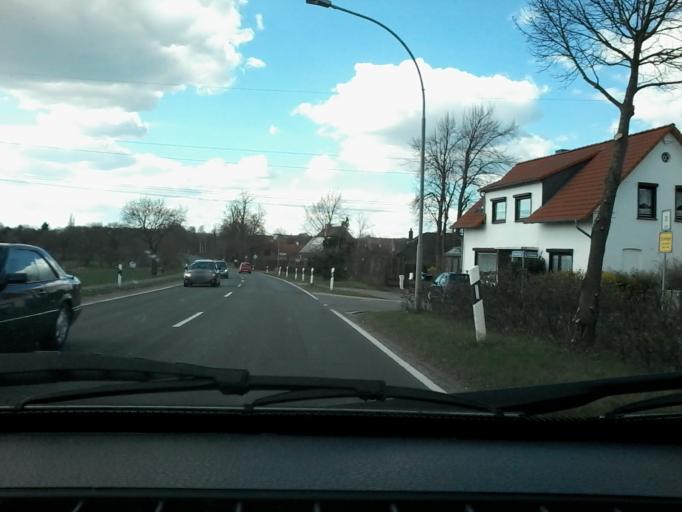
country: DE
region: Lower Saxony
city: Langwedel
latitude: 52.9926
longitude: 9.1322
